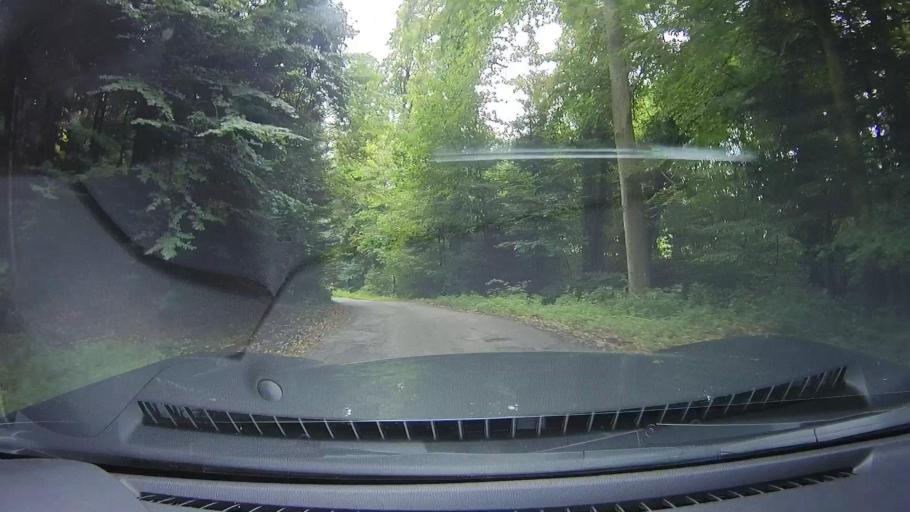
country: DE
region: Baden-Wuerttemberg
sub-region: Regierungsbezirk Stuttgart
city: Murrhardt
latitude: 48.9565
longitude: 9.5543
